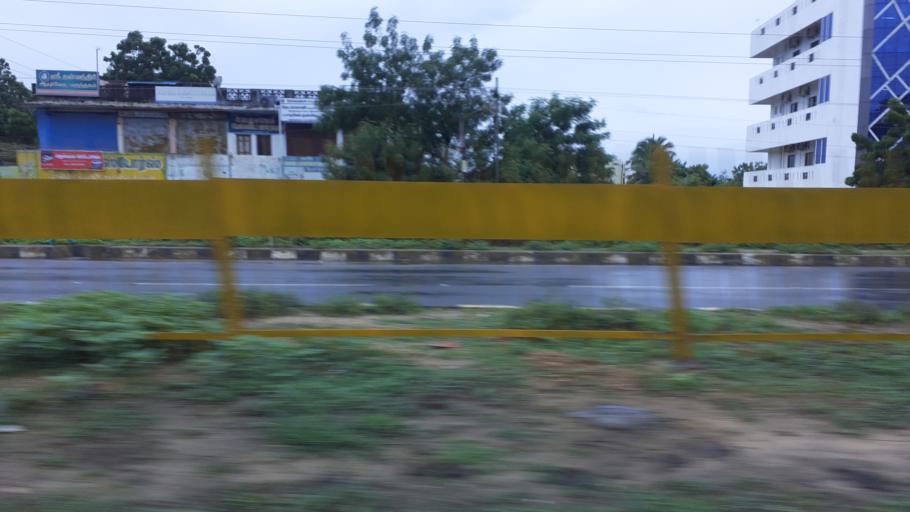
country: IN
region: Tamil Nadu
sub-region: Tirunelveli Kattabo
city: Tirunelveli
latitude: 8.7138
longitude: 77.7739
